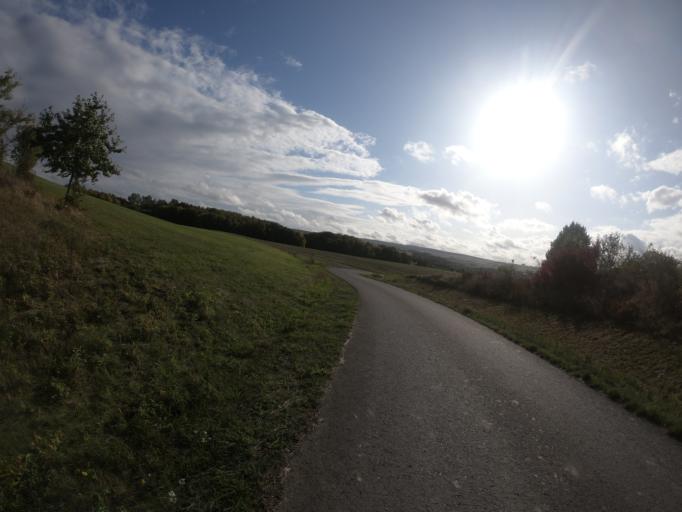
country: DE
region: Hesse
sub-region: Regierungsbezirk Giessen
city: Villmar
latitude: 50.3358
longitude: 8.1886
